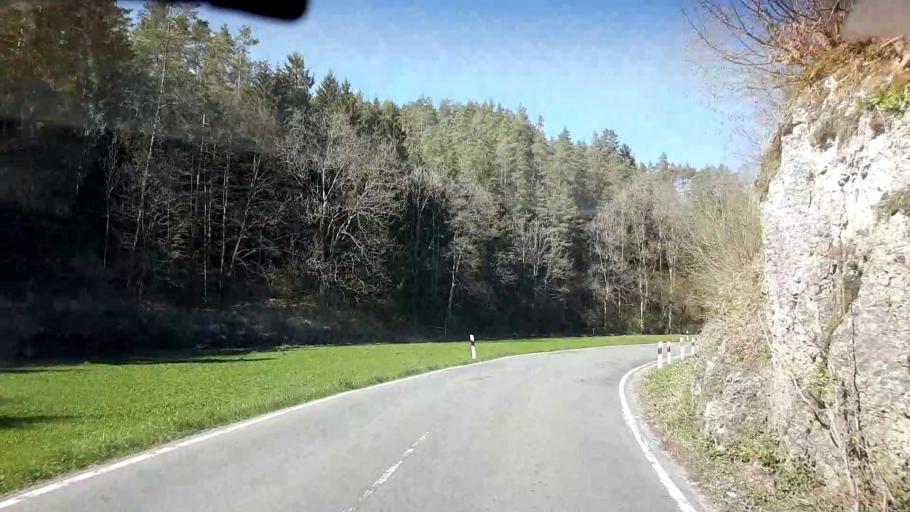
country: DE
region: Bavaria
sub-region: Upper Franconia
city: Pottenstein
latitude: 49.7821
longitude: 11.4183
